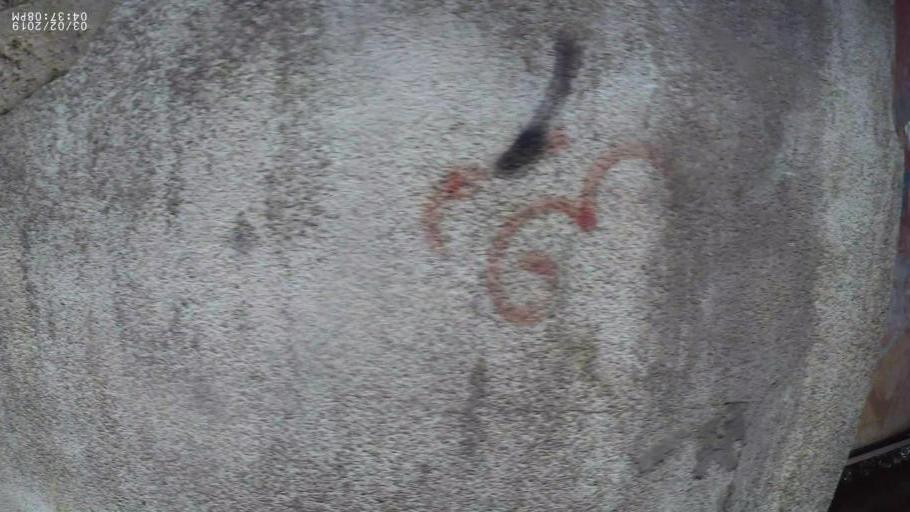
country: JO
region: Amman
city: Amman
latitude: 31.9653
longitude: 35.9247
